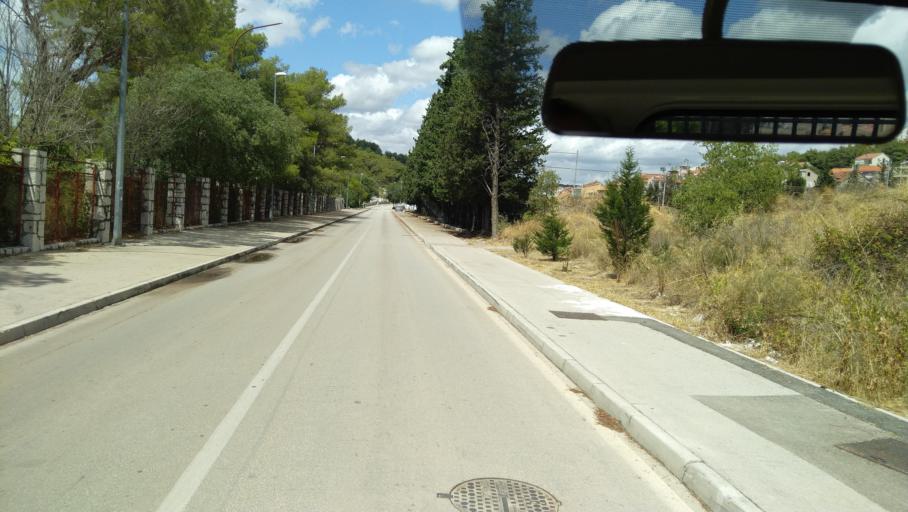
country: HR
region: Sibensko-Kniniska
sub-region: Grad Sibenik
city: Sibenik
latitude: 43.7450
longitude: 15.8861
